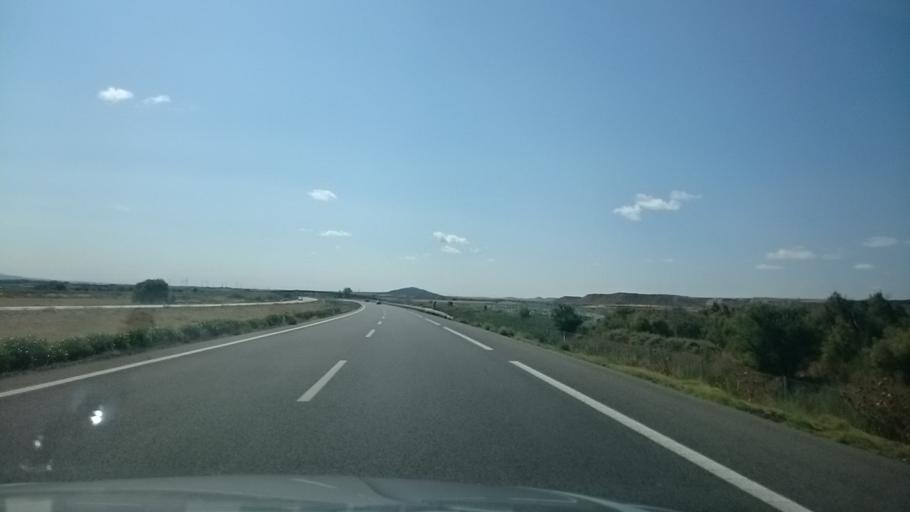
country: ES
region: Aragon
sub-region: Provincia de Zaragoza
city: Frescano
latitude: 41.9290
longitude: -1.4953
